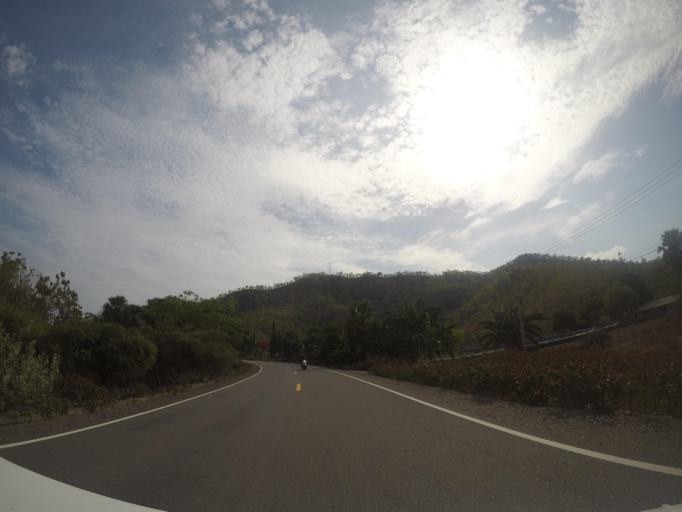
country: ID
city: Metinaro
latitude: -8.5365
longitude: 125.7075
